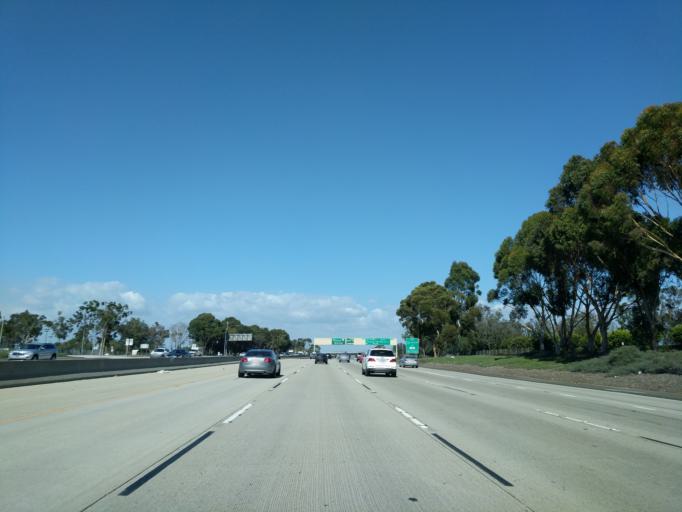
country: US
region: California
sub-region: Orange County
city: Costa Mesa
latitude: 33.6675
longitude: -117.8930
